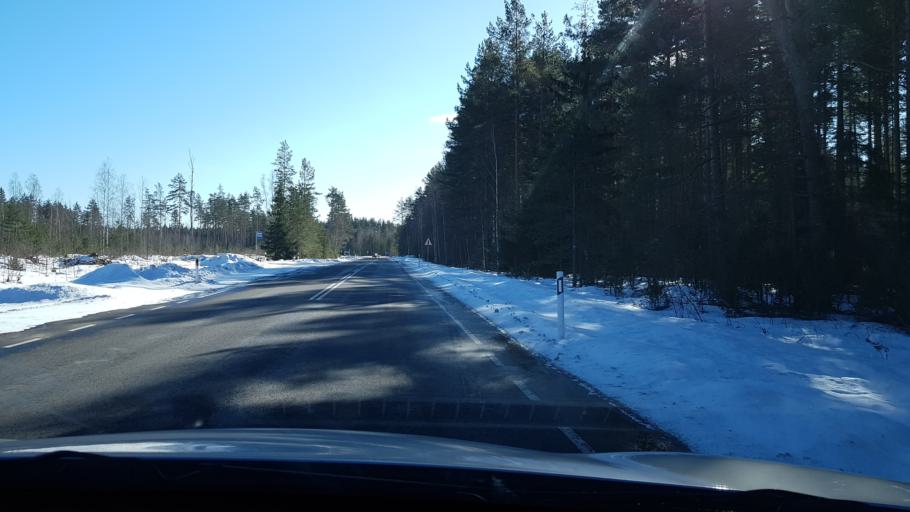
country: EE
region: Polvamaa
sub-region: Raepina vald
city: Rapina
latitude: 57.9854
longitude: 27.5655
